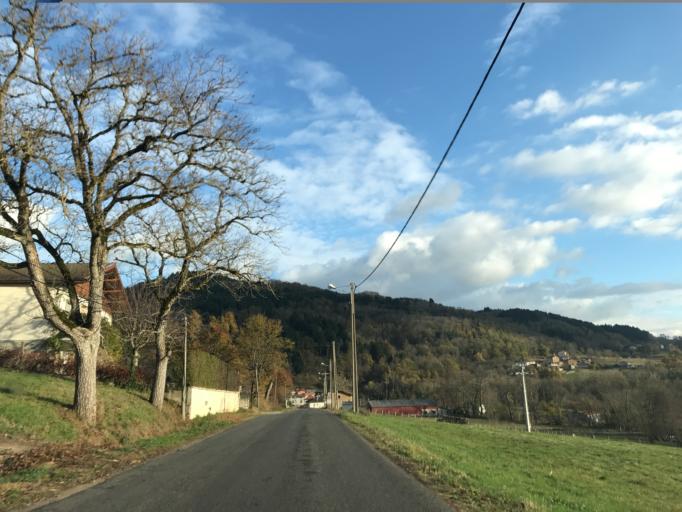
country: FR
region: Auvergne
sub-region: Departement du Puy-de-Dome
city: Courpiere
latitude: 45.7562
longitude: 3.6125
